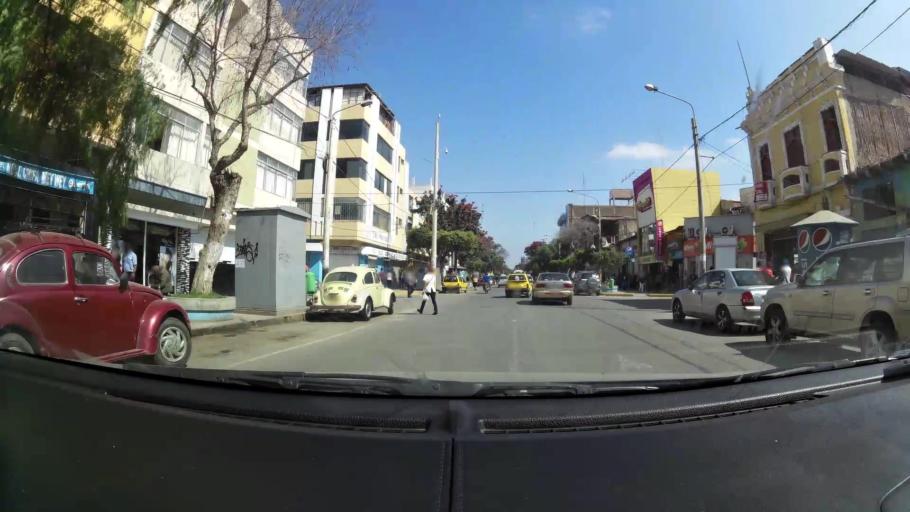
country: PE
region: Lambayeque
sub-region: Provincia de Chiclayo
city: Chiclayo
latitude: -6.7695
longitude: -79.8383
